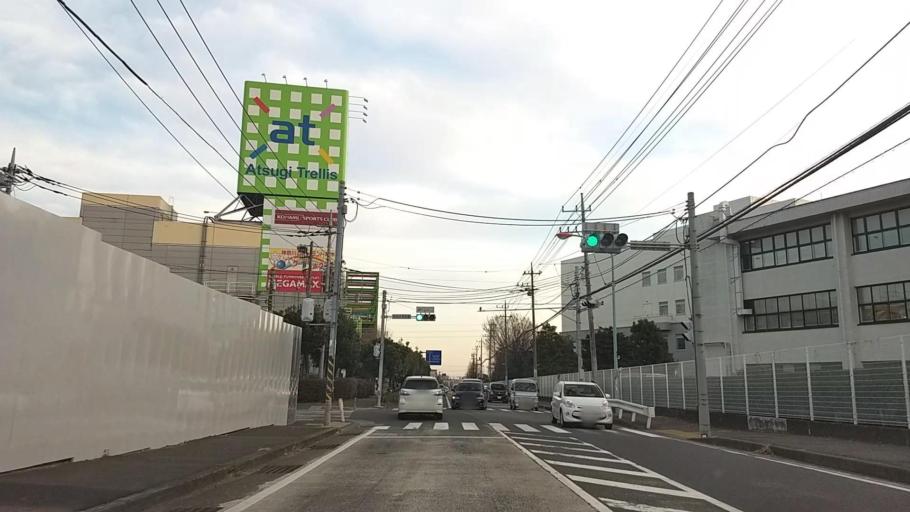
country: JP
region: Kanagawa
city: Atsugi
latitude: 35.4482
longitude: 139.3412
